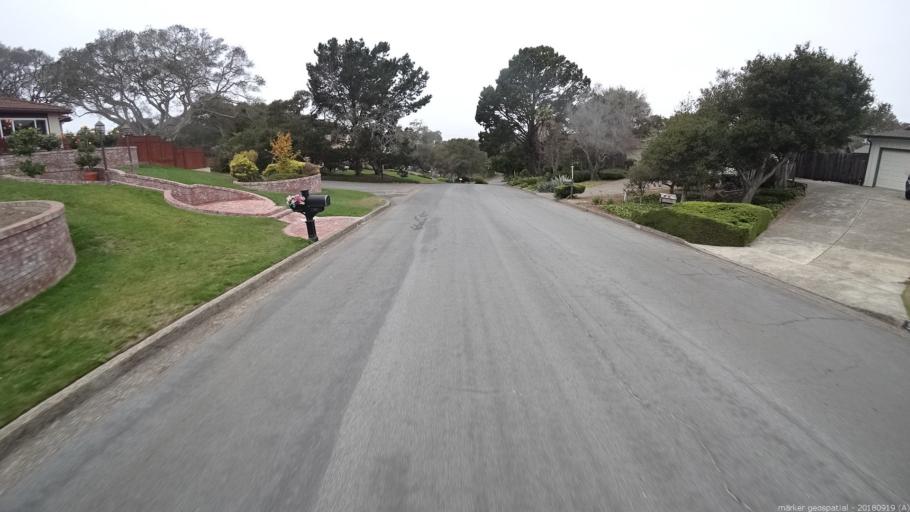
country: US
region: California
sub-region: Monterey County
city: Prunedale
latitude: 36.7795
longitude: -121.7113
